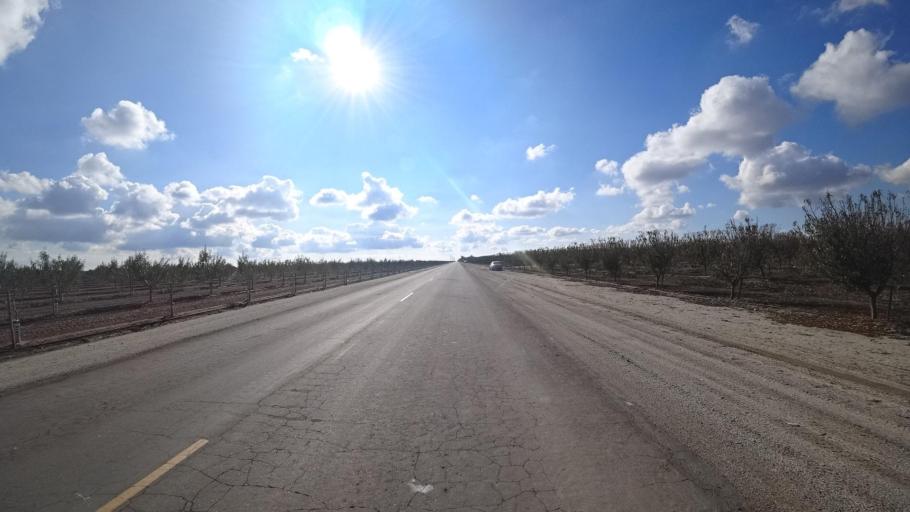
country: US
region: California
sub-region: Kern County
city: McFarland
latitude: 35.6571
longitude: -119.2322
